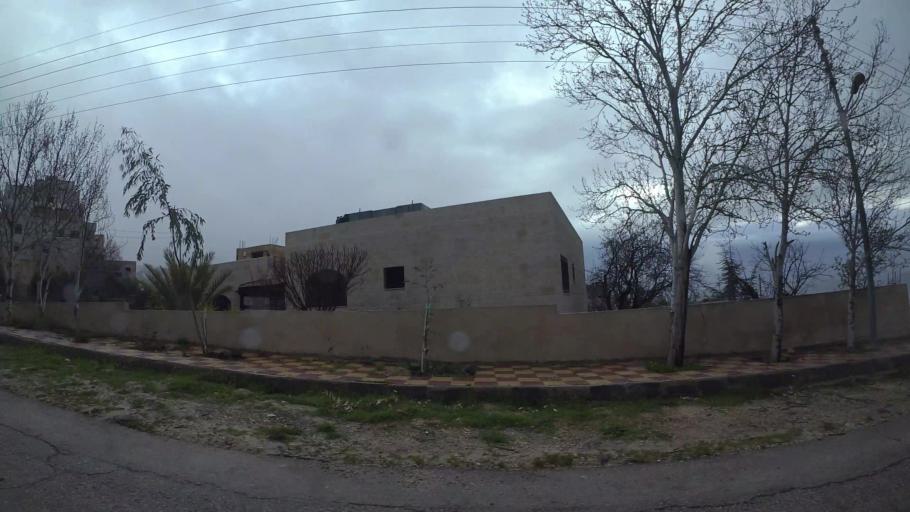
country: JO
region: Amman
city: Al Jubayhah
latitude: 32.0373
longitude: 35.8435
